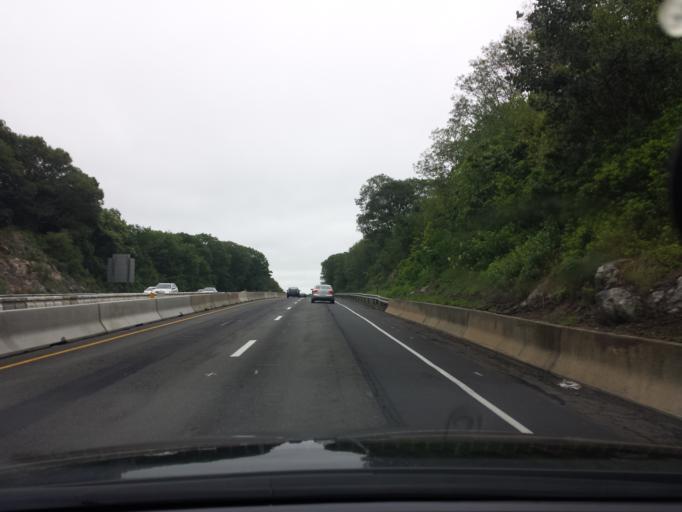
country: US
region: Connecticut
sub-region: Middlesex County
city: Old Saybrook Center
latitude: 41.3211
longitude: -72.3153
